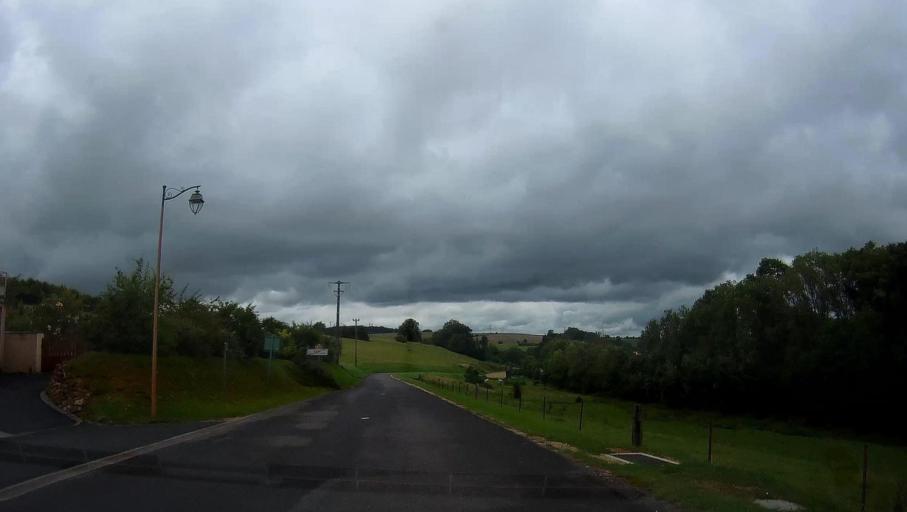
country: FR
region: Champagne-Ardenne
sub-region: Departement des Ardennes
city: Rimogne
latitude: 49.7738
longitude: 4.4682
